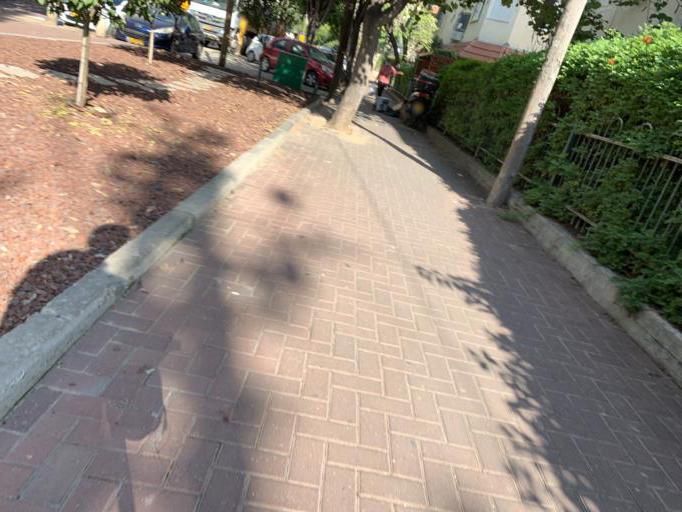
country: IL
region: Tel Aviv
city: Ramat Gan
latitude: 32.0880
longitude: 34.8062
